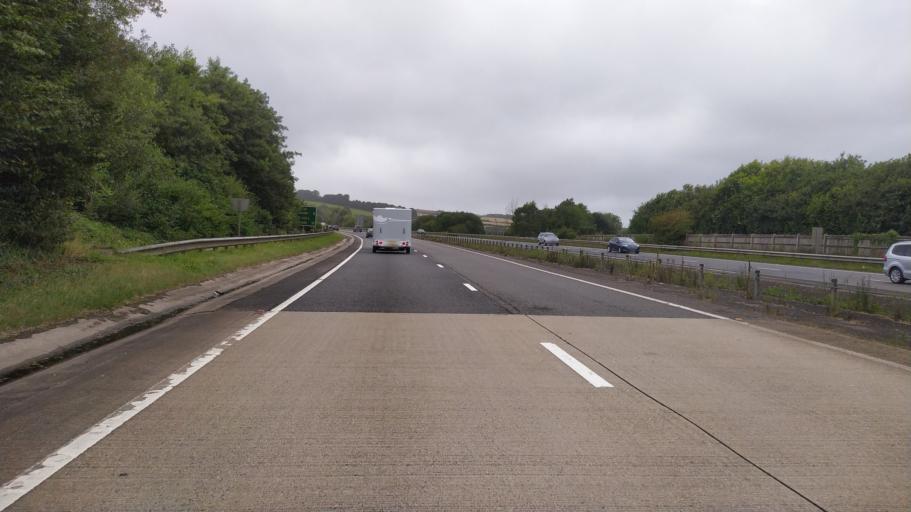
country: GB
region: England
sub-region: Dorset
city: Dorchester
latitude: 50.7531
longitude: -2.3494
